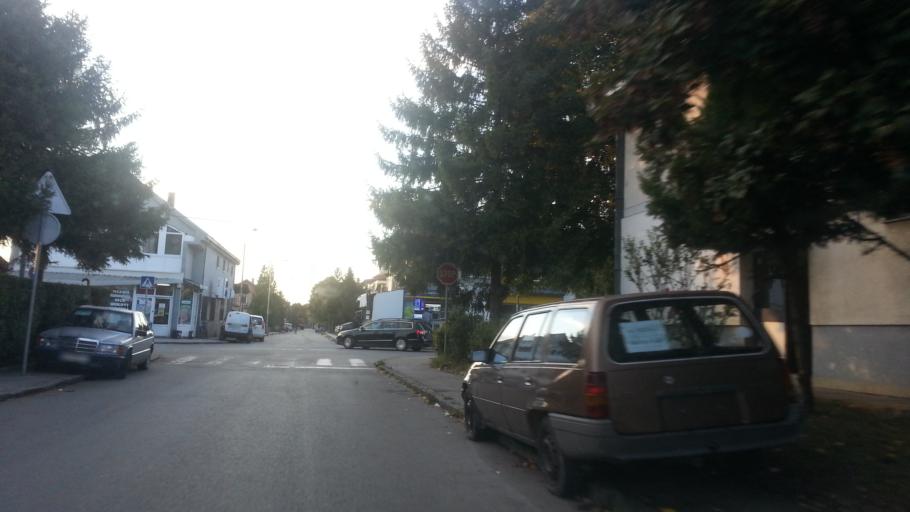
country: RS
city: Novi Banovci
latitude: 44.9028
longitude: 20.2828
